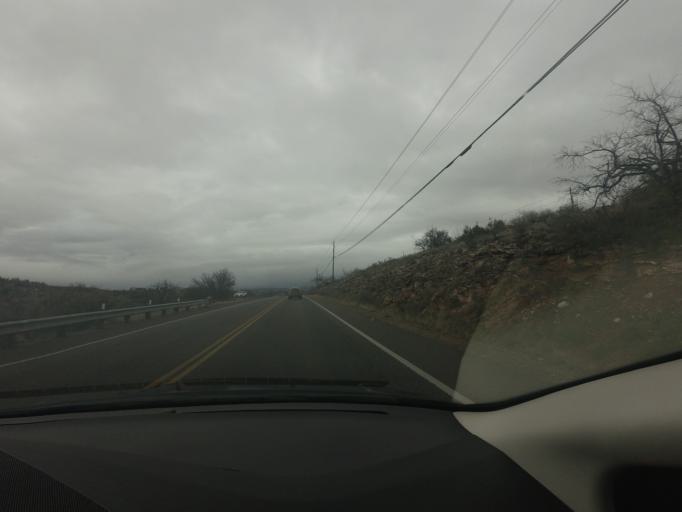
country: US
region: Arizona
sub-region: Yavapai County
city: Lake Montezuma
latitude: 34.6388
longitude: -111.8033
